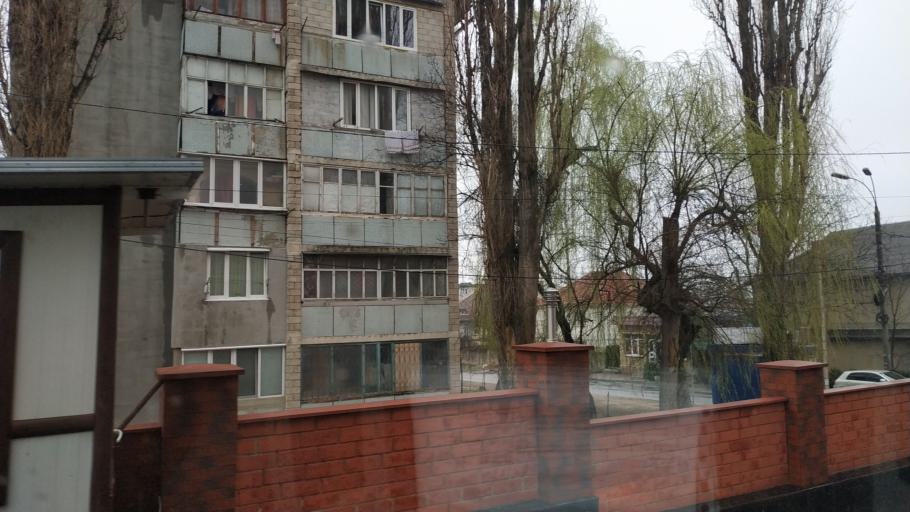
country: MD
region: Chisinau
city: Vatra
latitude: 47.0351
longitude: 28.7828
